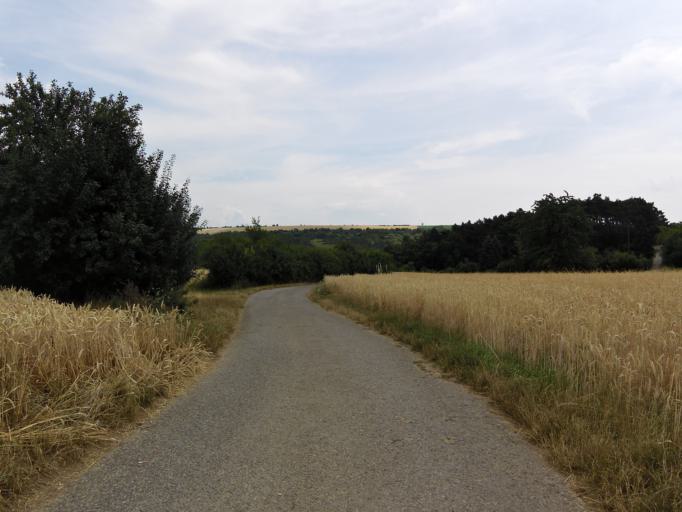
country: DE
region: Bavaria
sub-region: Regierungsbezirk Unterfranken
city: Gerbrunn
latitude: 49.7749
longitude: 9.9890
